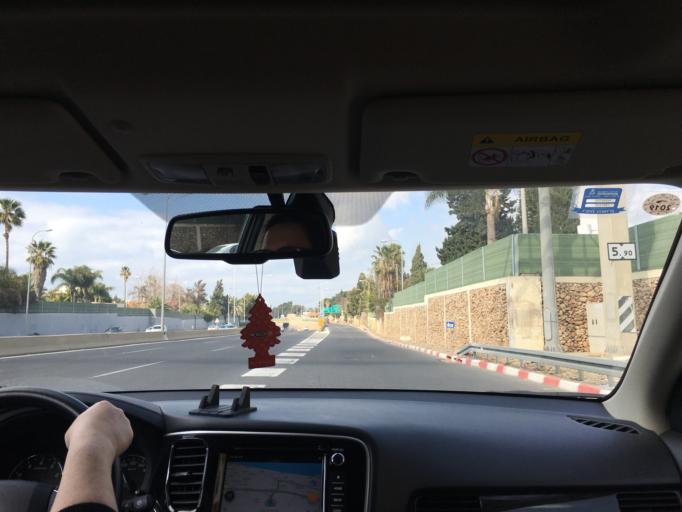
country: IL
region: Tel Aviv
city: Kefar Shemaryahu
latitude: 32.1755
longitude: 34.8161
